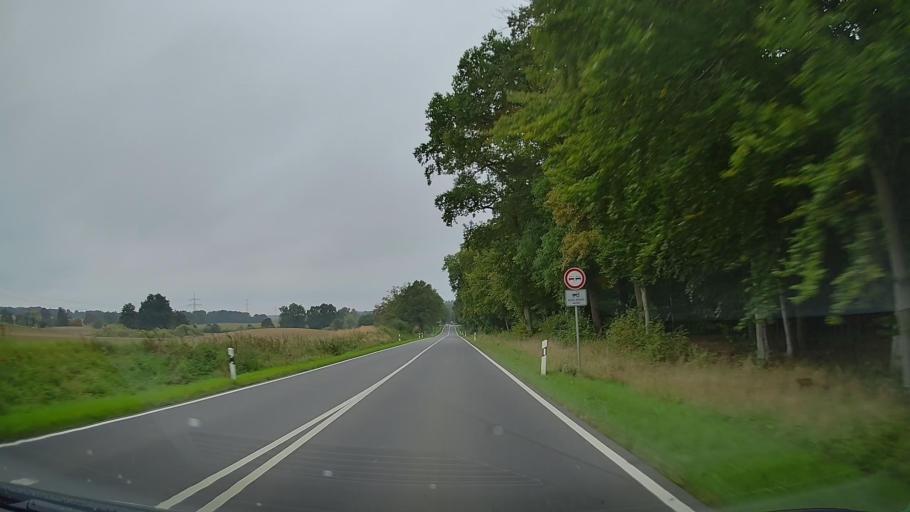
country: DE
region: Mecklenburg-Vorpommern
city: Tarnow
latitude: 53.7410
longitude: 12.0073
